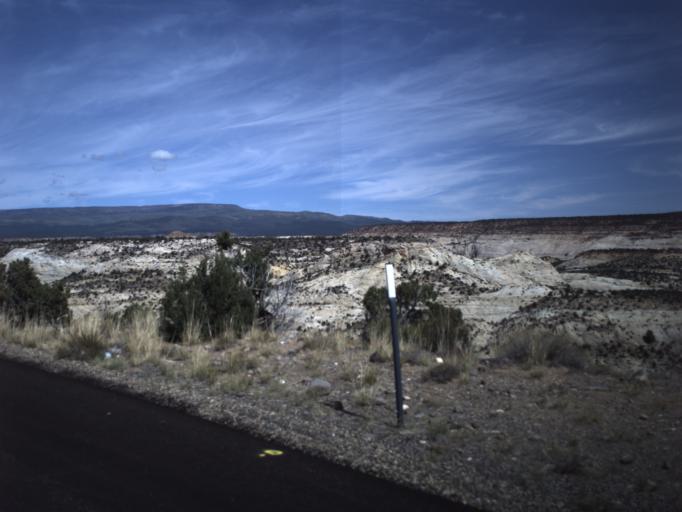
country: US
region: Utah
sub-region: Wayne County
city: Loa
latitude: 37.8415
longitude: -111.4219
